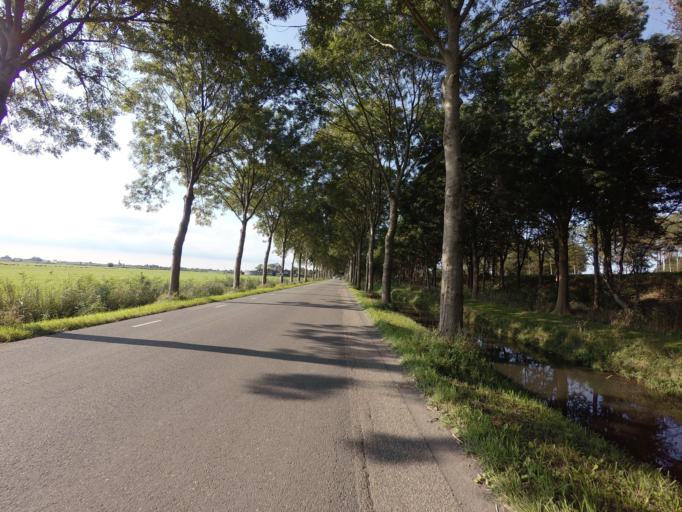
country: NL
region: North Holland
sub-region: Gemeente Hoorn
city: Hoorn
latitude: 52.6637
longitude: 5.1481
